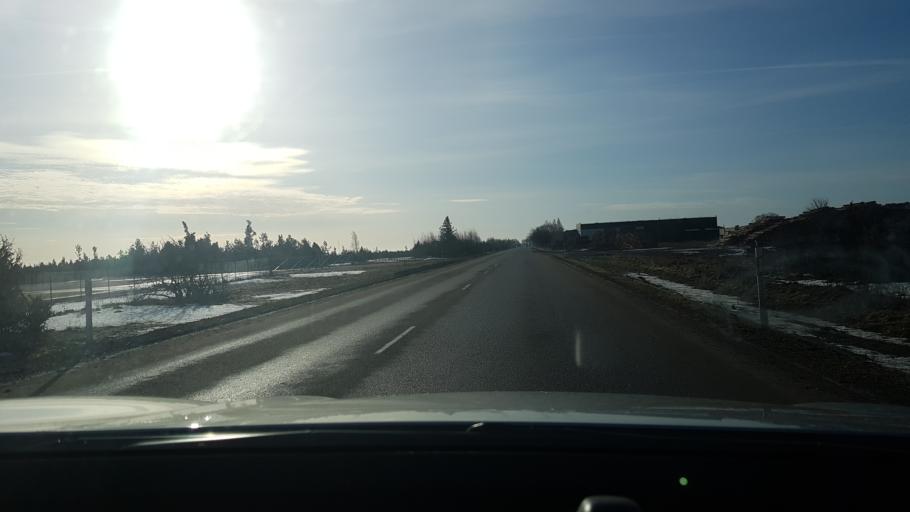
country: EE
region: Saare
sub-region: Kuressaare linn
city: Kuressaare
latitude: 58.2295
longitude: 22.5050
